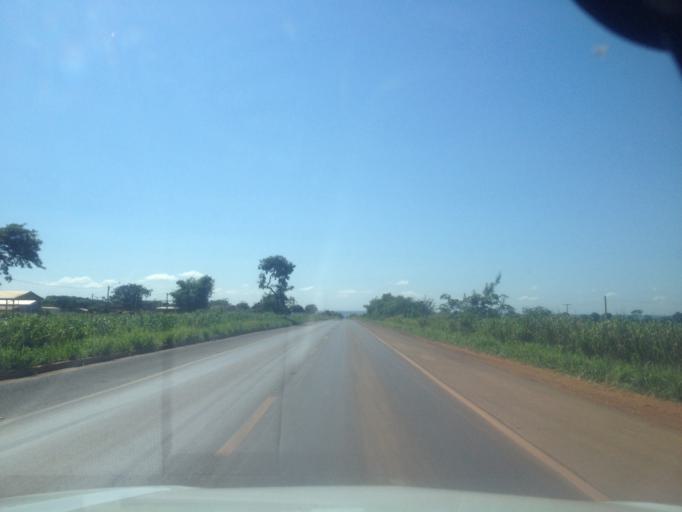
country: BR
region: Minas Gerais
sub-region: Santa Vitoria
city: Santa Vitoria
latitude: -18.9952
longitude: -50.5669
